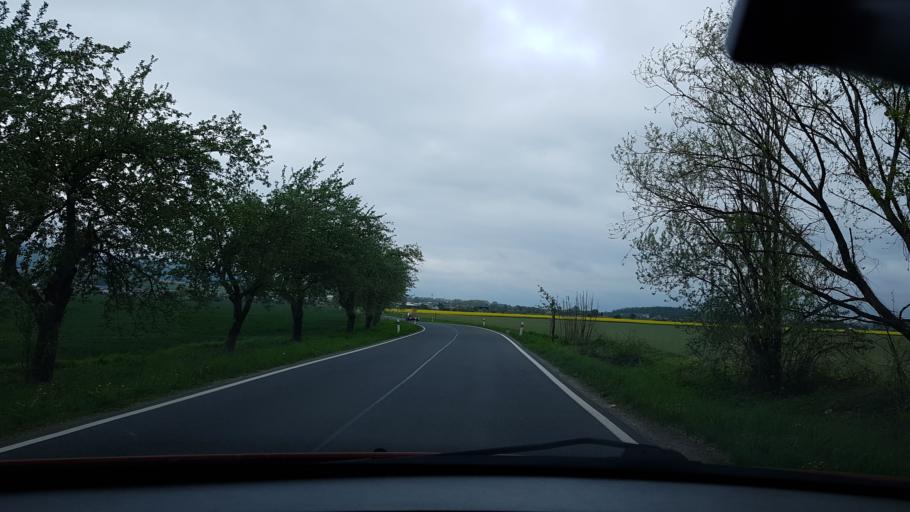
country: CZ
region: Olomoucky
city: Javornik
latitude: 50.3879
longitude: 17.0350
